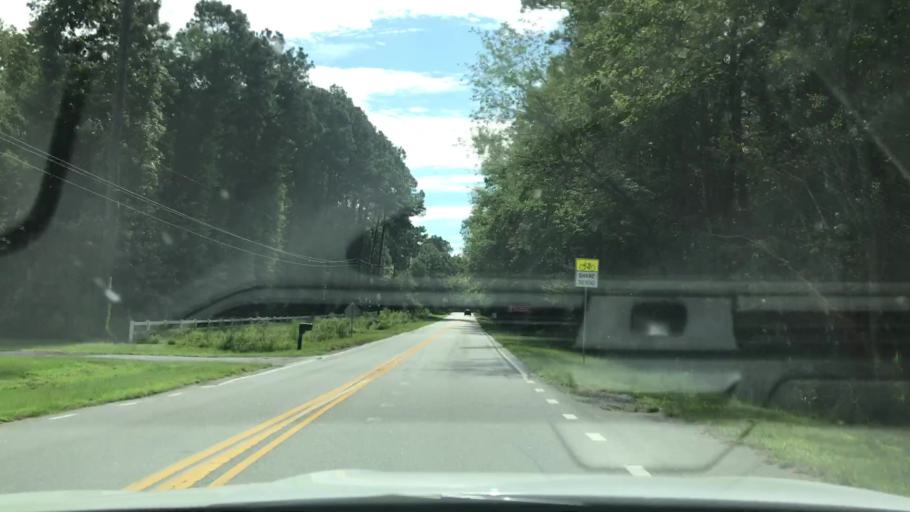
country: US
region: South Carolina
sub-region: Dorchester County
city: Centerville
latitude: 32.9465
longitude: -80.2008
